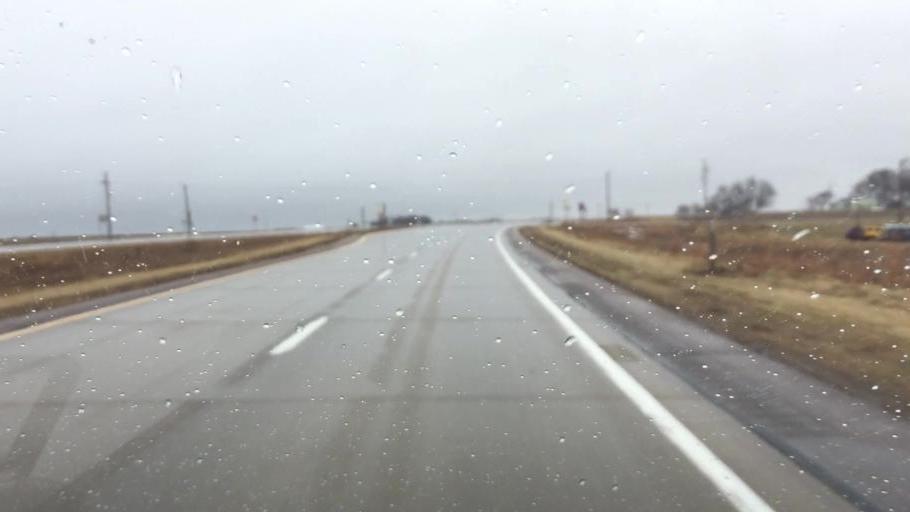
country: US
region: Iowa
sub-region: O'Brien County
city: Sheldon
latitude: 43.0704
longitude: -95.8969
